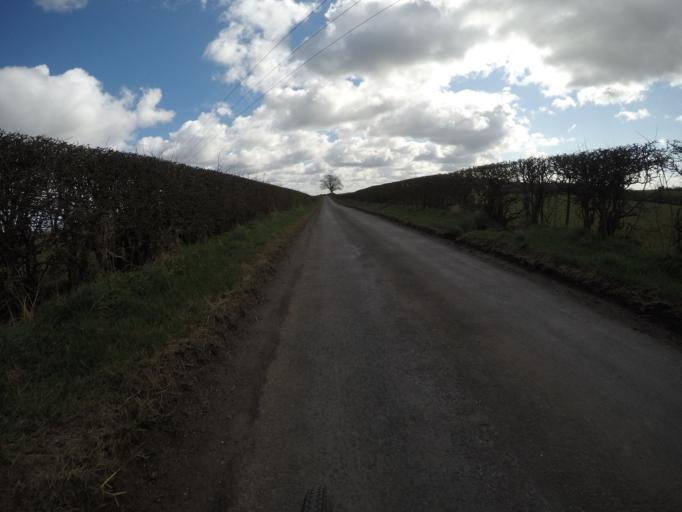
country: GB
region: Scotland
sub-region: South Ayrshire
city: Dundonald
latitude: 55.5896
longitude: -4.5916
